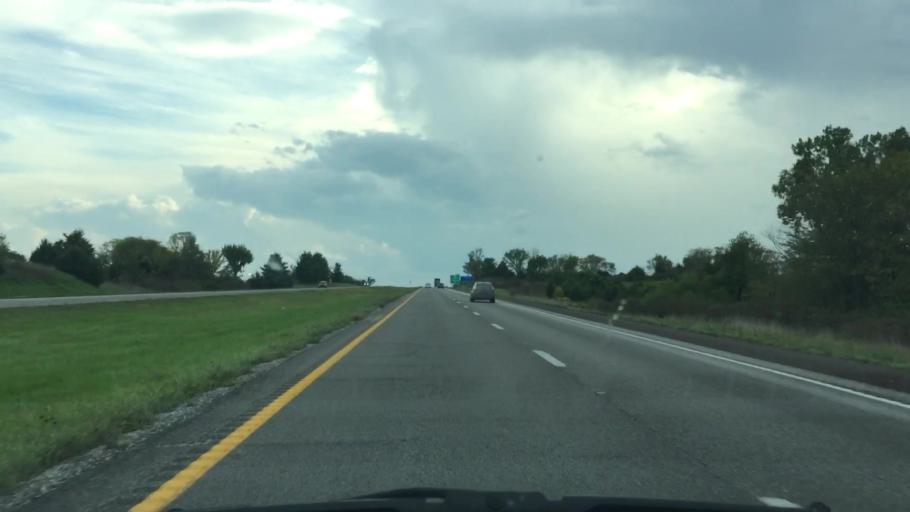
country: US
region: Missouri
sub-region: Clinton County
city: Cameron
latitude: 39.8630
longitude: -94.1727
